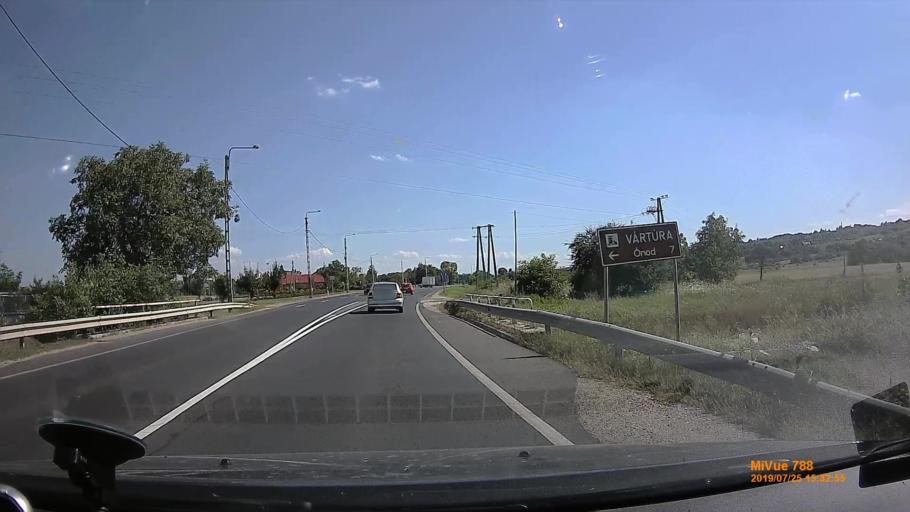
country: HU
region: Borsod-Abauj-Zemplen
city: Malyi
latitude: 48.0011
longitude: 20.8312
